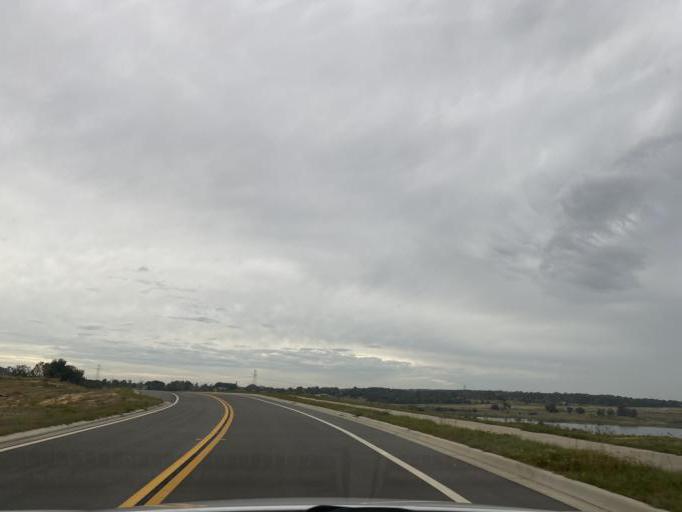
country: US
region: Florida
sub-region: Orange County
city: Oakland
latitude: 28.5372
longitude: -81.6909
